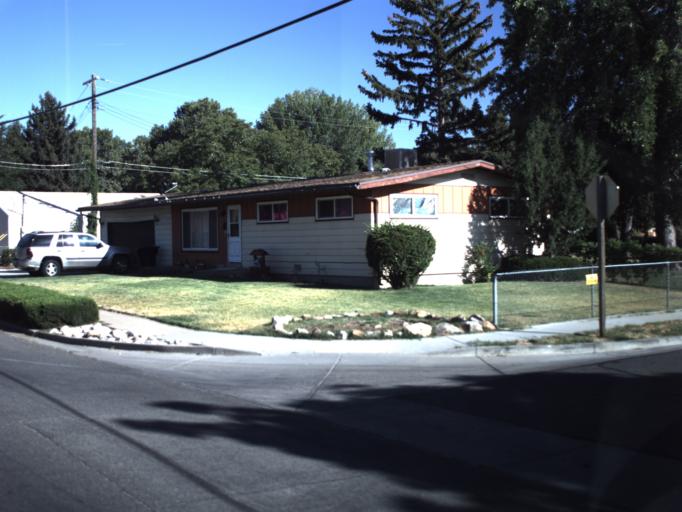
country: US
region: Utah
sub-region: Davis County
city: Sunset
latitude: 41.1399
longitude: -112.0341
